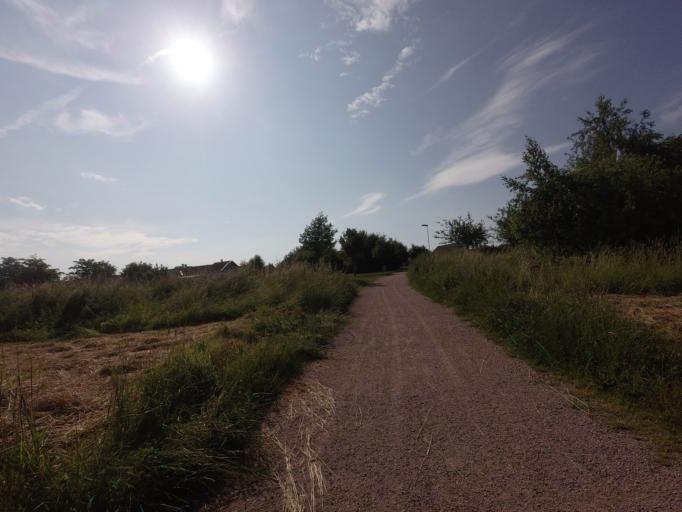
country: SE
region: Skane
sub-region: Trelleborgs Kommun
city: Trelleborg
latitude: 55.3610
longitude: 13.2292
